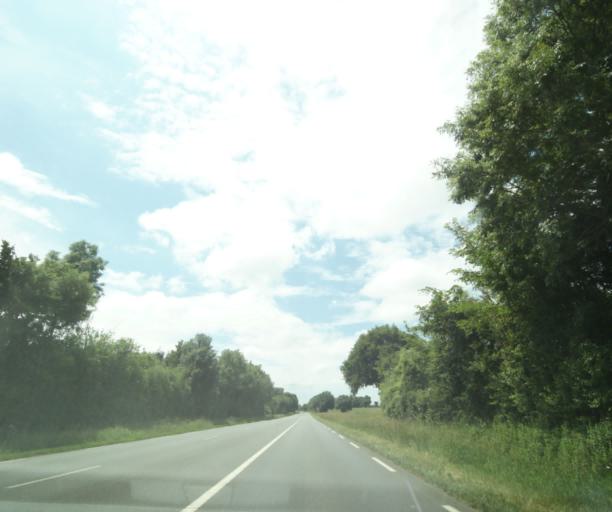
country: FR
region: Poitou-Charentes
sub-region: Departement des Deux-Sevres
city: Champdeniers-Saint-Denis
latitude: 46.4500
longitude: -0.3853
